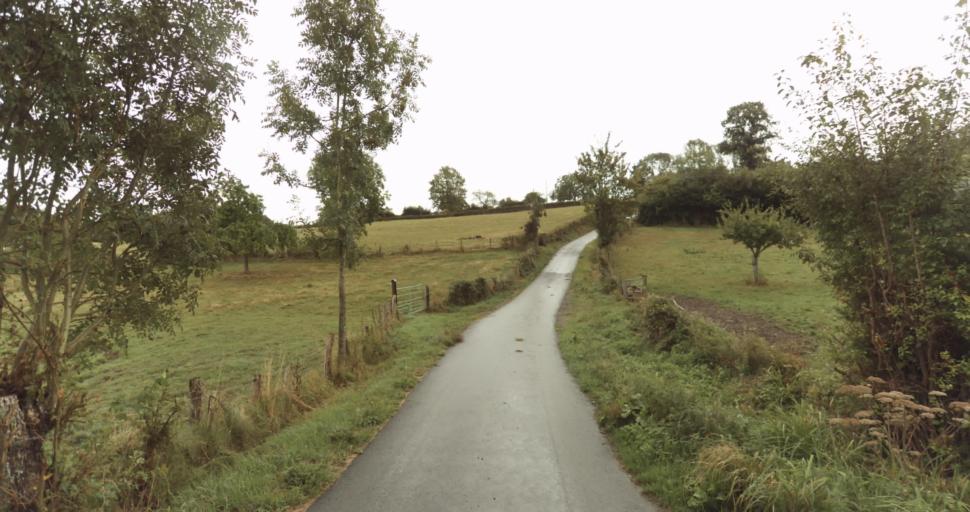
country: FR
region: Lower Normandy
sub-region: Departement de l'Orne
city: Vimoutiers
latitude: 48.8676
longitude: 0.1984
